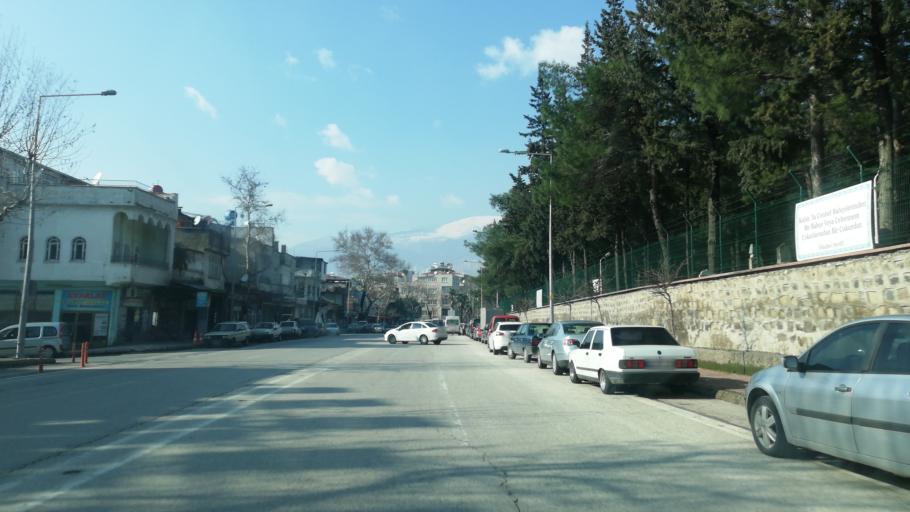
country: TR
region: Kahramanmaras
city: Kahramanmaras
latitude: 37.5765
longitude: 36.9347
